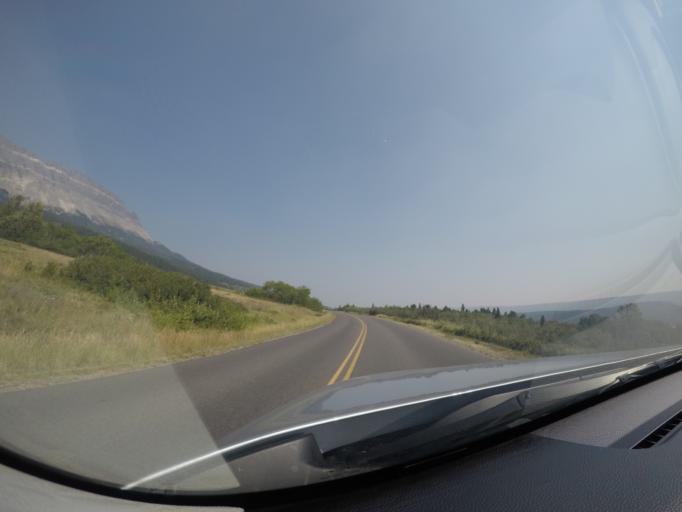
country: US
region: Montana
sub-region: Glacier County
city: North Browning
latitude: 48.7151
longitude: -113.4770
